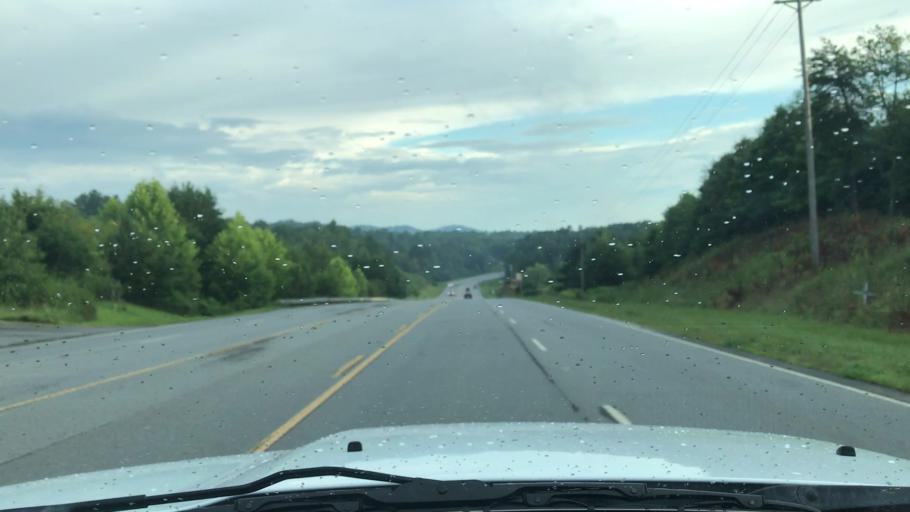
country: US
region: North Carolina
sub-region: Cherokee County
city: Murphy
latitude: 35.0191
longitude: -84.1204
